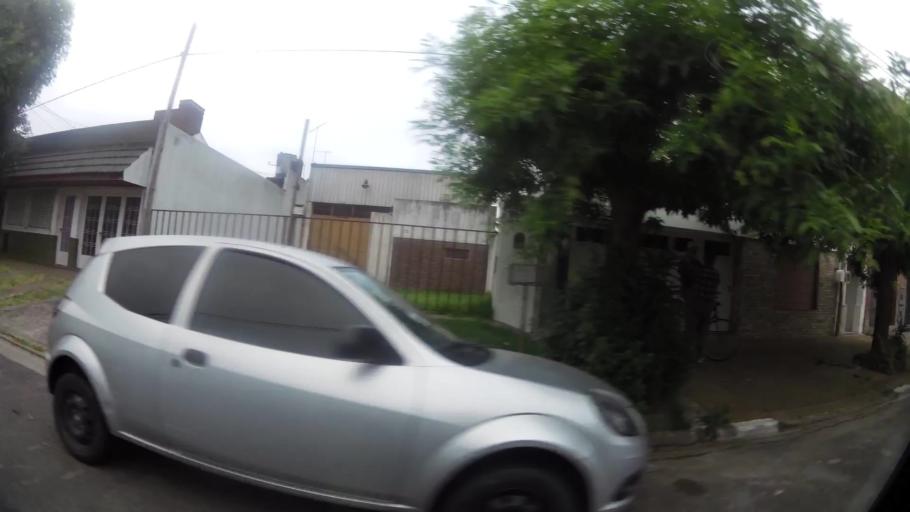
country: AR
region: Buenos Aires
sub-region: Partido de La Plata
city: La Plata
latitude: -34.9184
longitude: -57.9793
